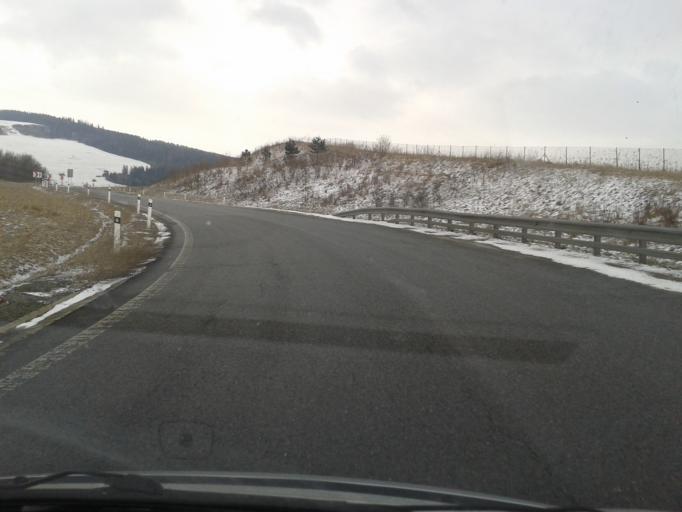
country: SK
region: Zilinsky
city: Tvrdosin
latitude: 49.3444
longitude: 19.5795
